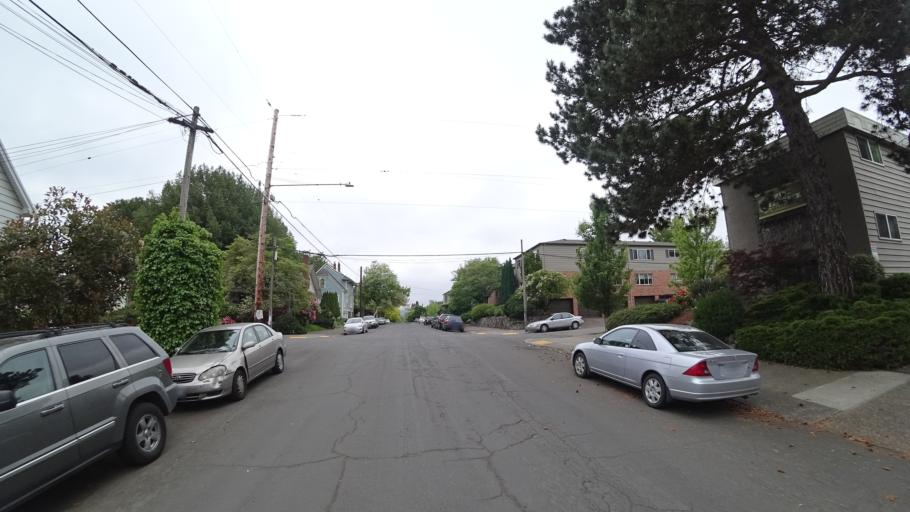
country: US
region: Oregon
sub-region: Multnomah County
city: Portland
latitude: 45.5207
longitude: -122.6327
